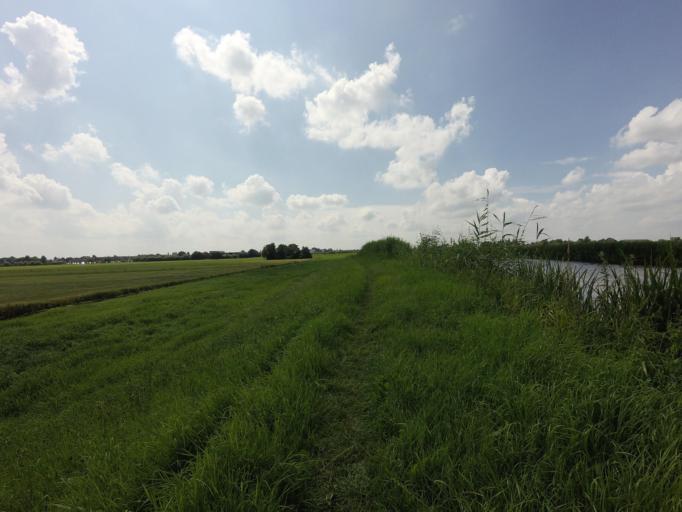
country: NL
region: South Holland
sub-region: Gemeente Vlist
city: Haastrecht
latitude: 52.0506
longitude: 4.7999
